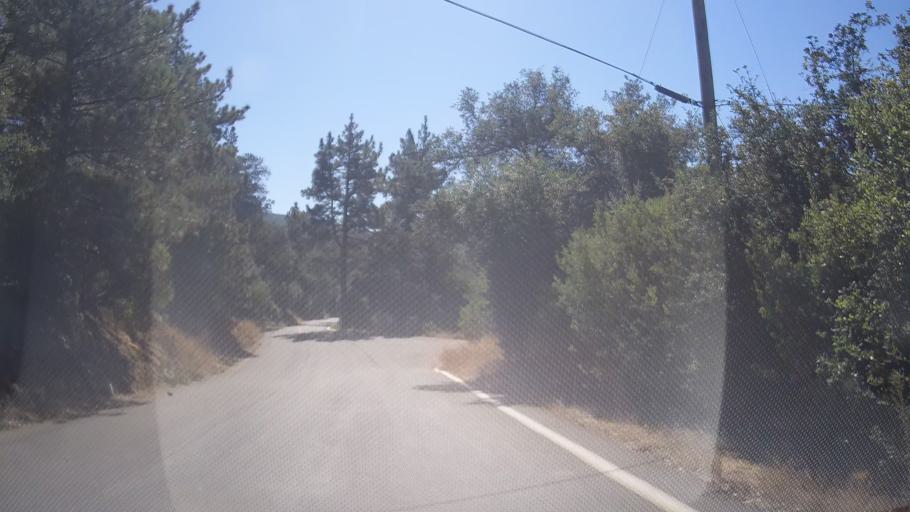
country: US
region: California
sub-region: San Diego County
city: Julian
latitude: 33.0378
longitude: -116.6362
